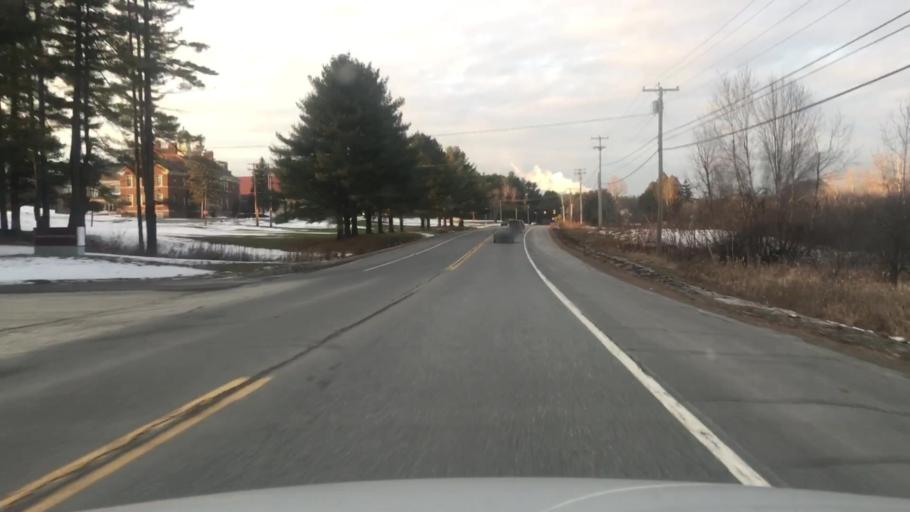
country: US
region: Maine
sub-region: Somerset County
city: Fairfield
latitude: 44.6671
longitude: -69.6288
